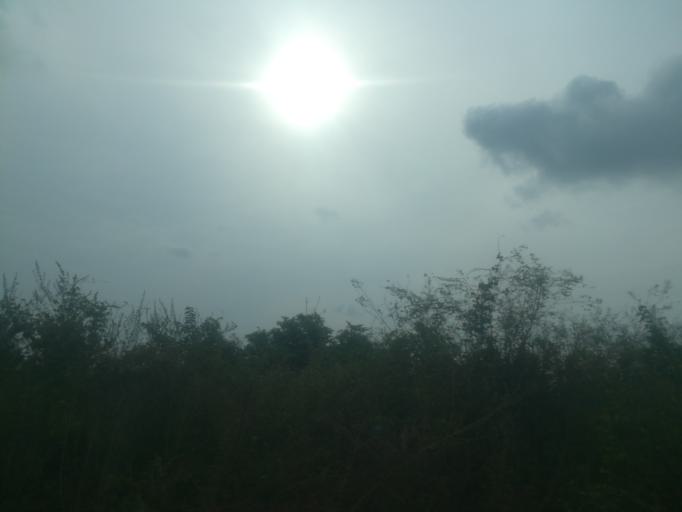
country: NG
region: Ogun
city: Ayetoro
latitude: 7.2981
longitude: 3.0768
